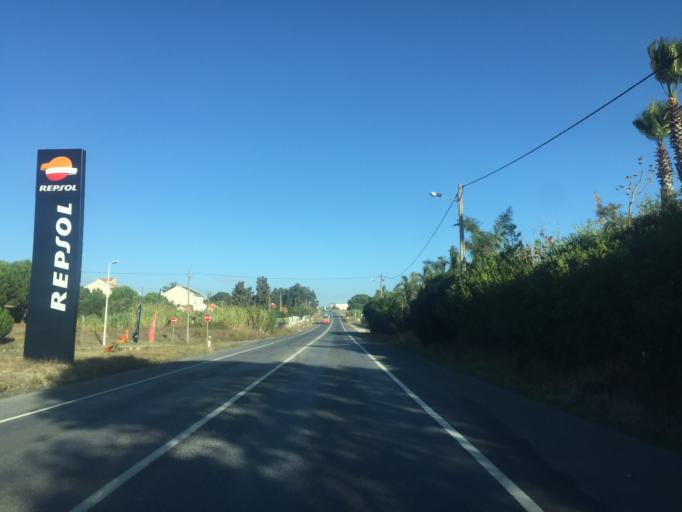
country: PT
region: Lisbon
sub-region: Azambuja
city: Aveiras de Cima
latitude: 39.1577
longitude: -8.9139
